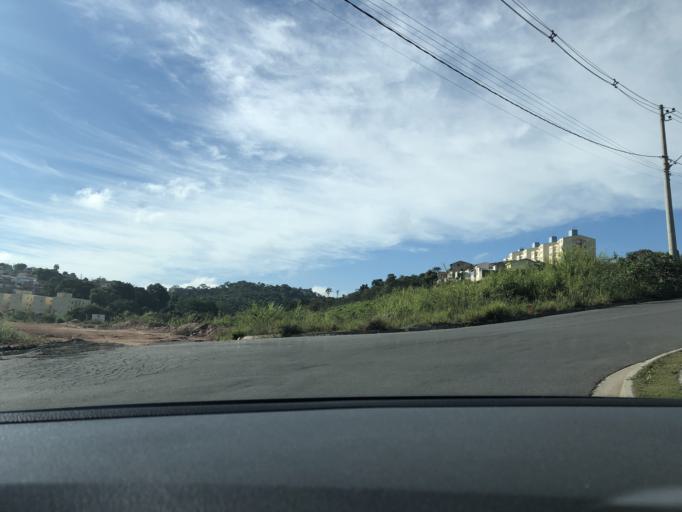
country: BR
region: Sao Paulo
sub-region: Campo Limpo Paulista
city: Campo Limpo Paulista
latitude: -23.2109
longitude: -46.8039
